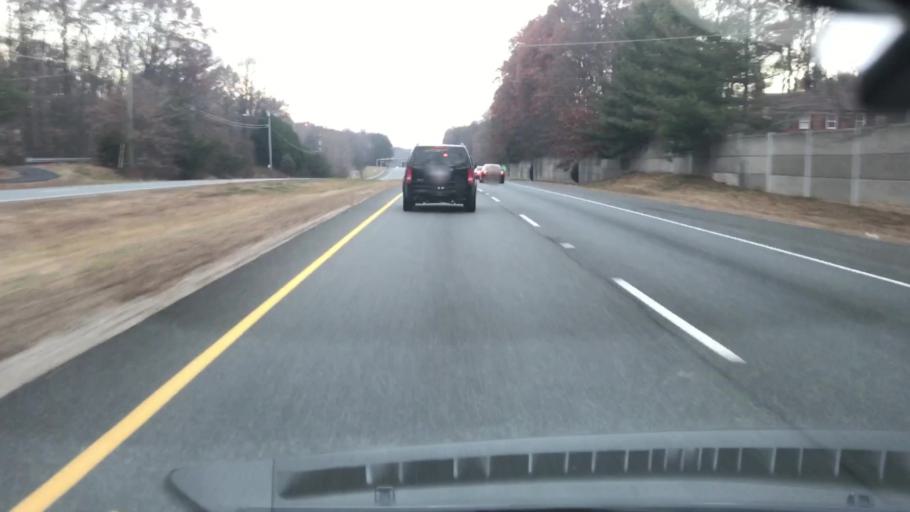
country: US
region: Virginia
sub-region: Fairfax County
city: Burke
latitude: 38.7657
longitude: -77.2848
